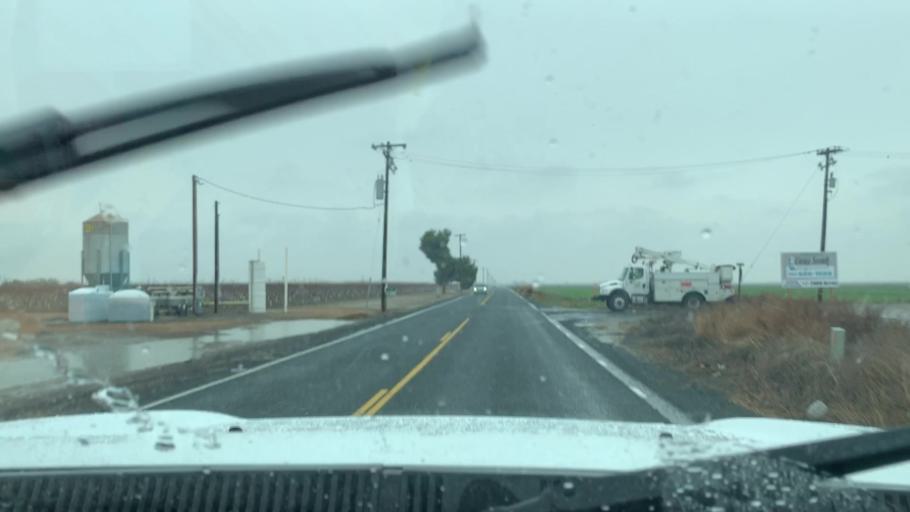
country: US
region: California
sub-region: Tulare County
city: Earlimart
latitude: 35.8917
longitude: -119.3752
